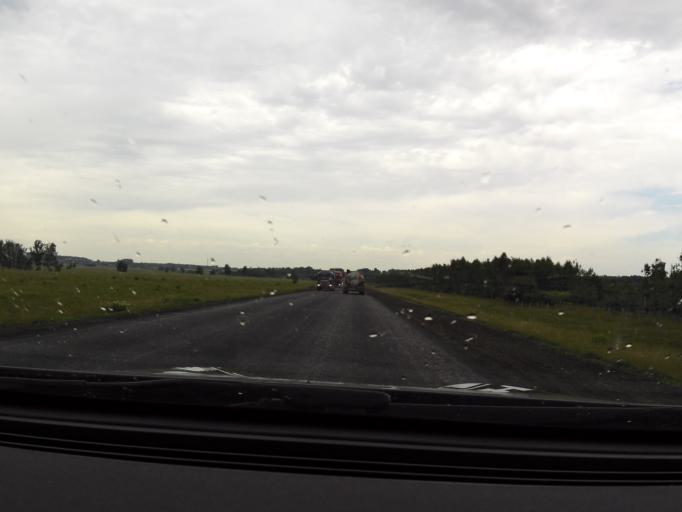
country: RU
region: Bashkortostan
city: Iglino
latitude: 54.7904
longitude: 56.5590
